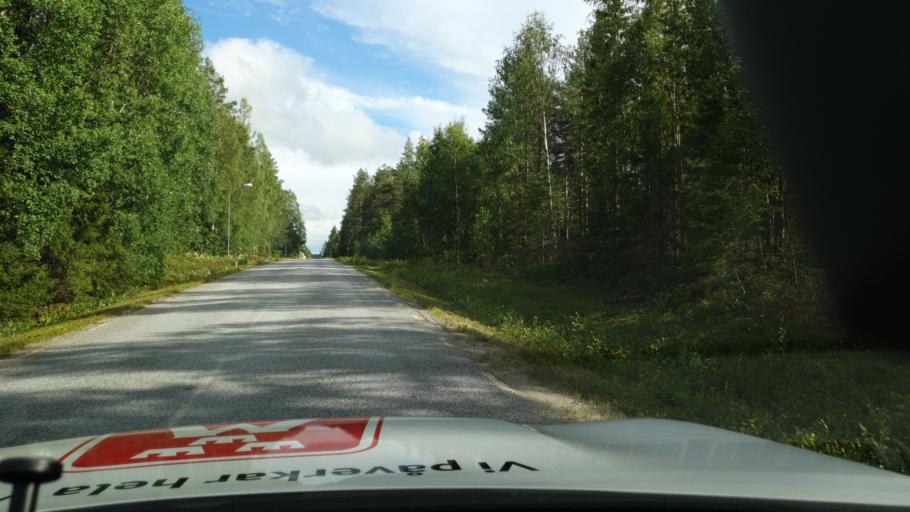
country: SE
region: Vaesterbotten
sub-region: Skelleftea Kommun
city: Burea
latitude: 64.4858
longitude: 21.0363
